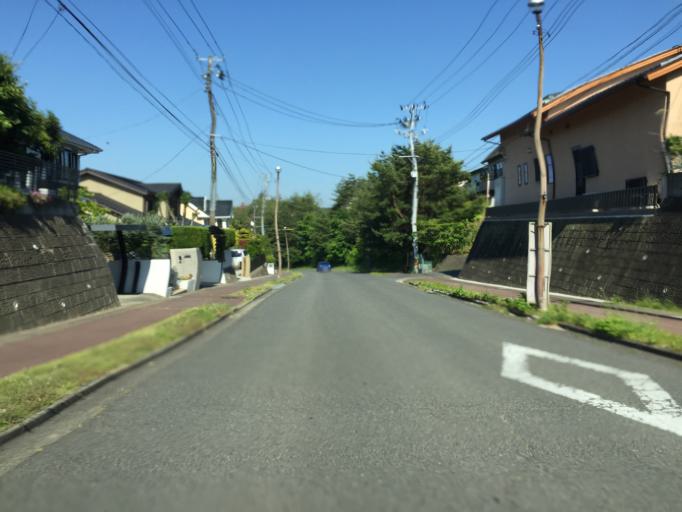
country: JP
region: Fukushima
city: Iwaki
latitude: 36.9646
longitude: 140.8598
